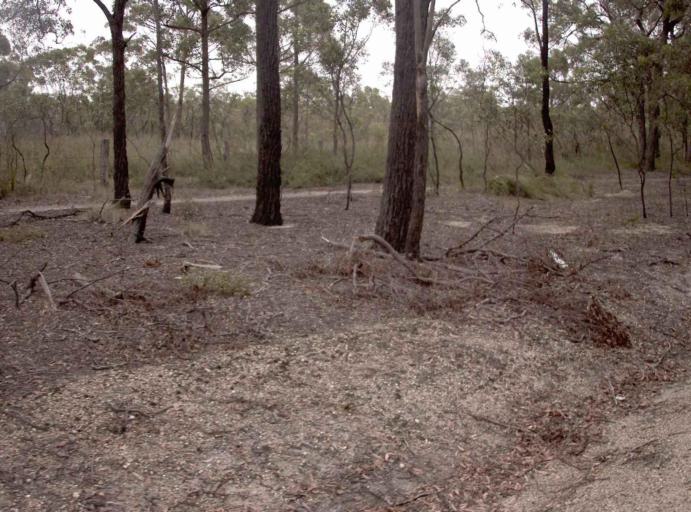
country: AU
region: Victoria
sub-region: Wellington
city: Heyfield
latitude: -37.9477
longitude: 146.7666
